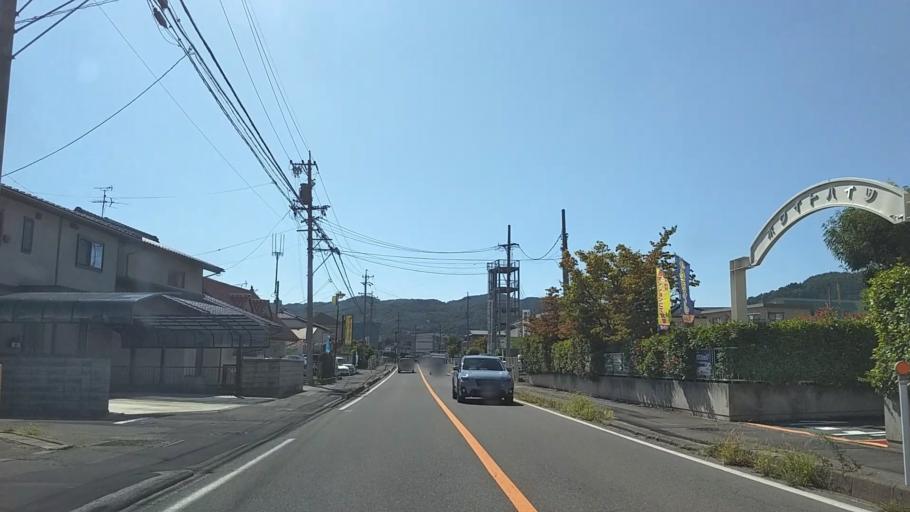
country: JP
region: Nagano
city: Nagano-shi
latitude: 36.6236
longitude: 138.1475
